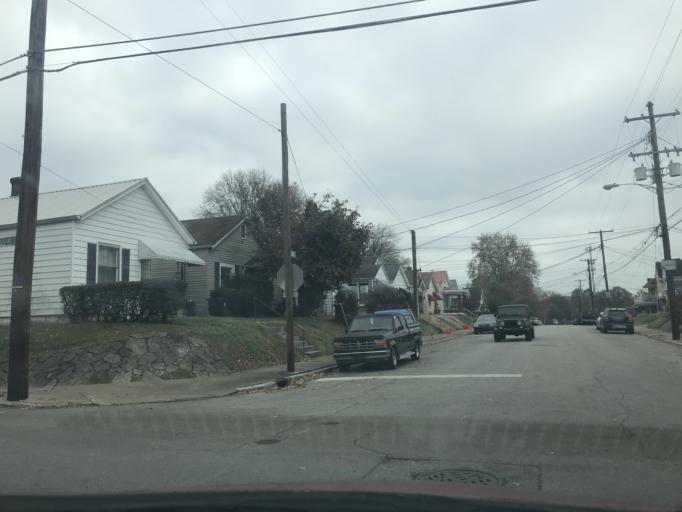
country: US
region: Kentucky
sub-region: Jefferson County
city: Louisville
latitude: 38.2373
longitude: -85.7312
